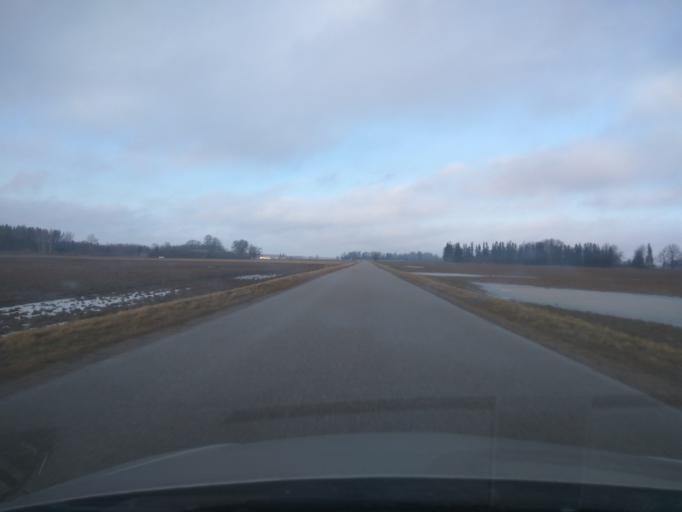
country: LV
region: Saldus Rajons
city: Saldus
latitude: 56.7879
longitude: 22.3873
